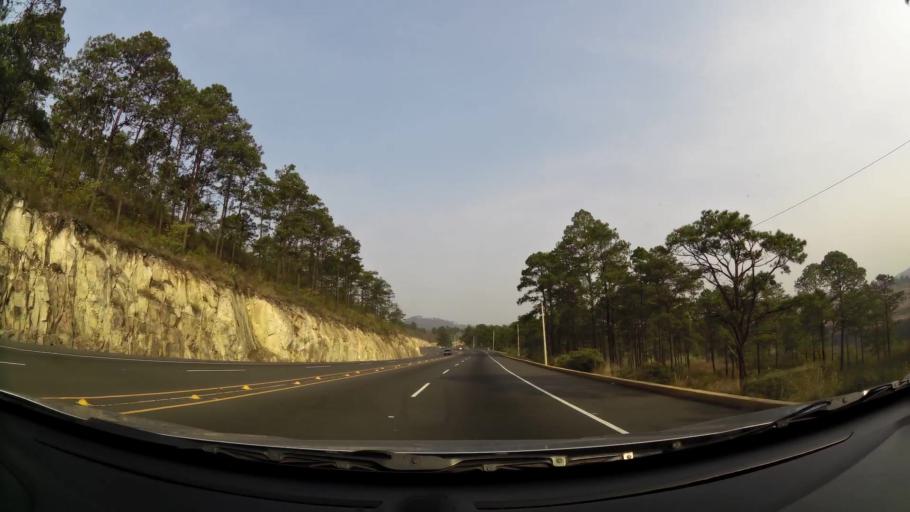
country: HN
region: Francisco Morazan
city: Zambrano
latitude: 14.2516
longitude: -87.3804
